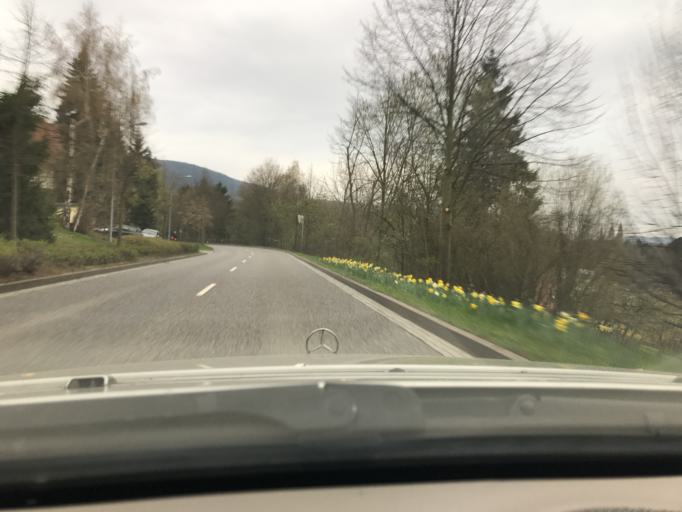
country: DE
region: Thuringia
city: Heilbad Heiligenstadt
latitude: 51.3810
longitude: 10.1501
